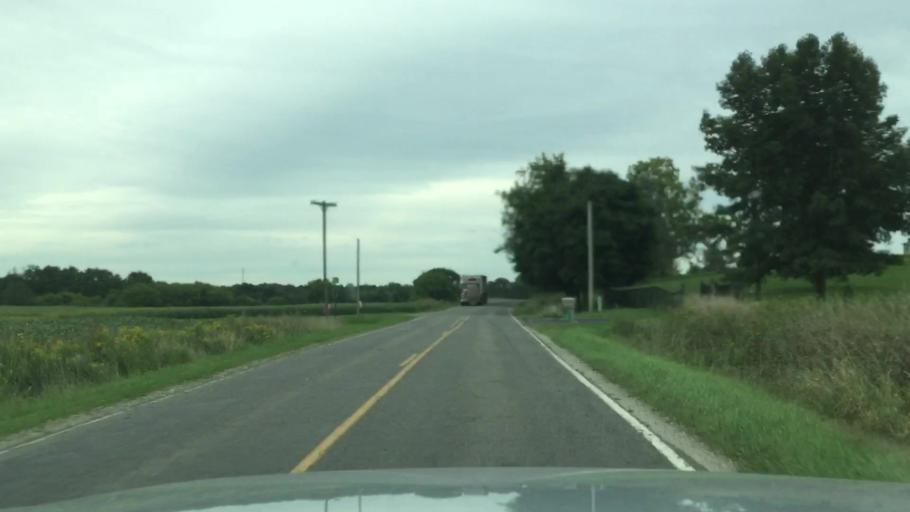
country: US
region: Michigan
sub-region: Shiawassee County
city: Durand
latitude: 42.8574
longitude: -84.0401
